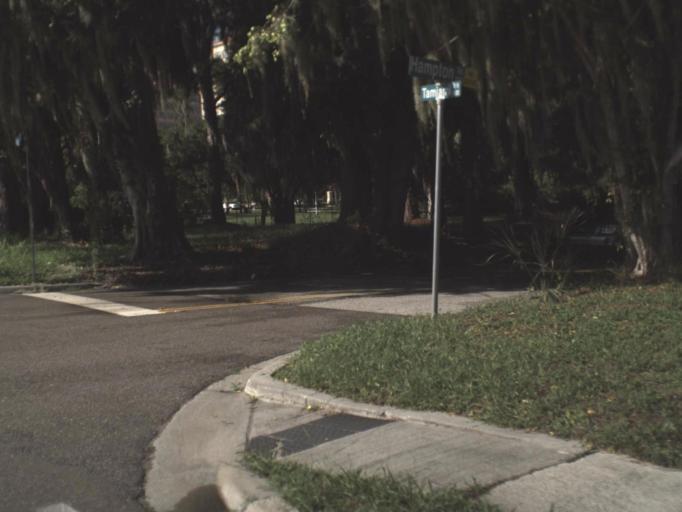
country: US
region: Florida
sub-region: Sarasota County
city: Sarasota
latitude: 27.3514
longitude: -82.5470
